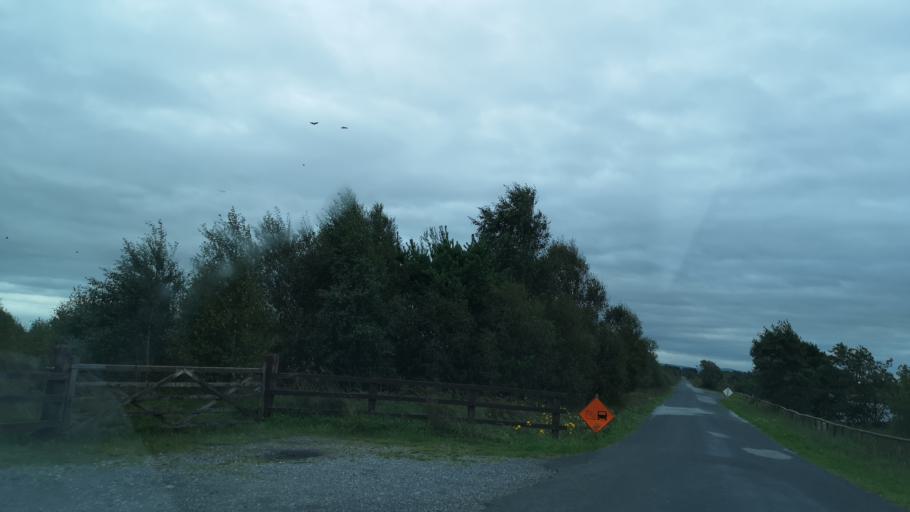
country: IE
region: Leinster
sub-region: Uibh Fhaili
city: Ferbane
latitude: 53.2202
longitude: -7.7268
